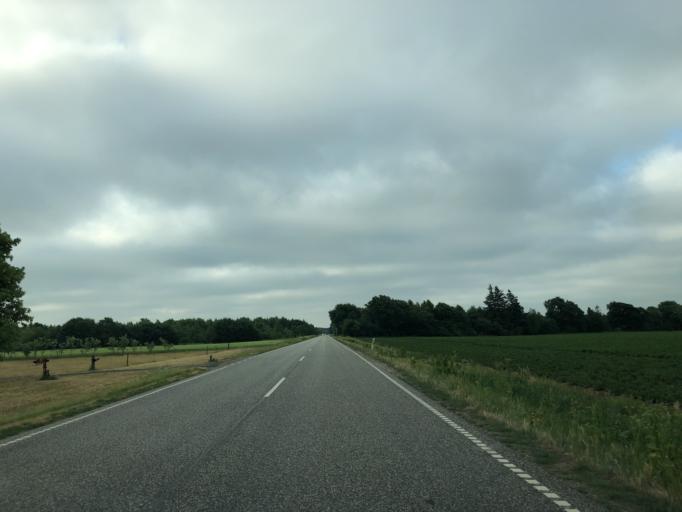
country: DK
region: South Denmark
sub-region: Vejle Kommune
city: Give
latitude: 55.8962
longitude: 9.2073
